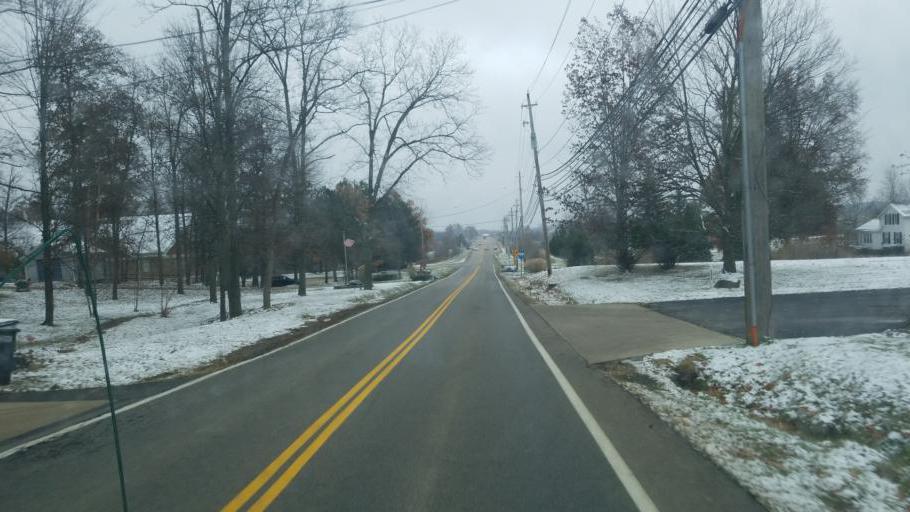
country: US
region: Ohio
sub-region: Cuyahoga County
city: Brecksville
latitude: 41.2894
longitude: -81.6422
